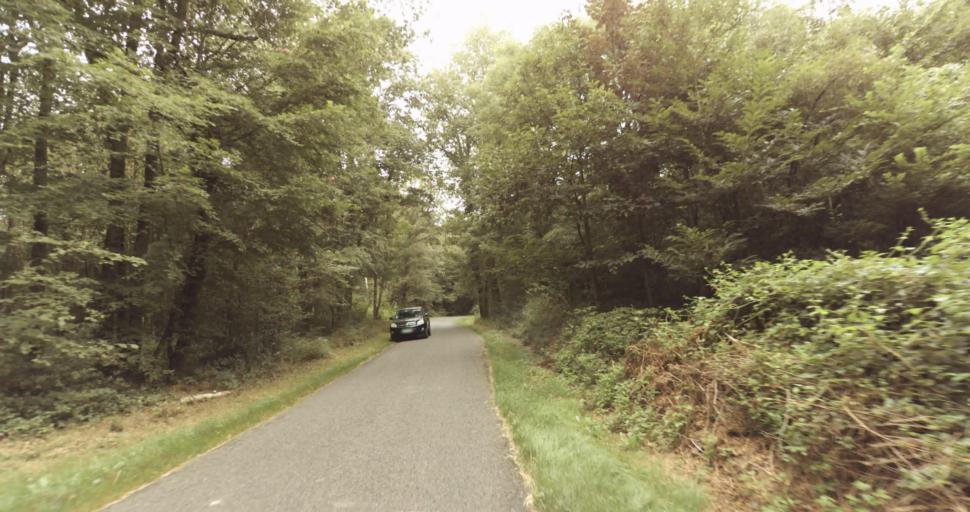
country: FR
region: Centre
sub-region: Departement d'Eure-et-Loir
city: Vert-en-Drouais
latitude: 48.8026
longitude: 1.2998
